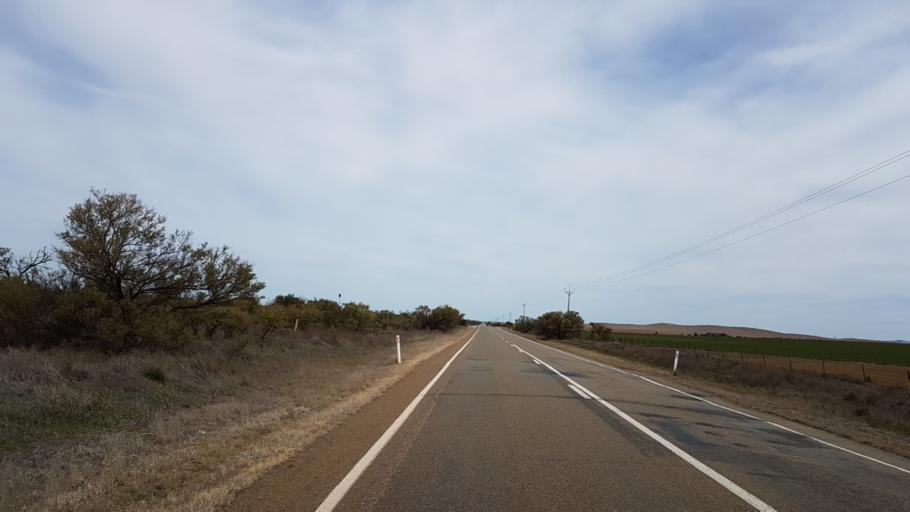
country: AU
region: South Australia
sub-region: Peterborough
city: Peterborough
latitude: -33.0024
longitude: 138.7755
